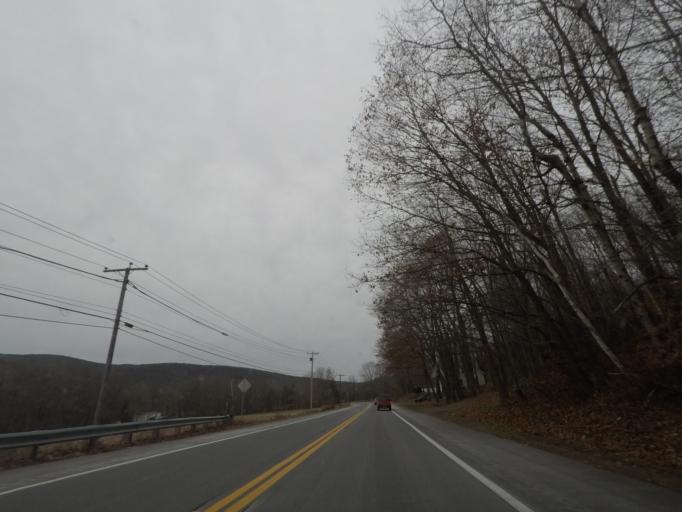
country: US
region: Massachusetts
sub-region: Berkshire County
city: Lanesborough
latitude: 42.5515
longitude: -73.3083
